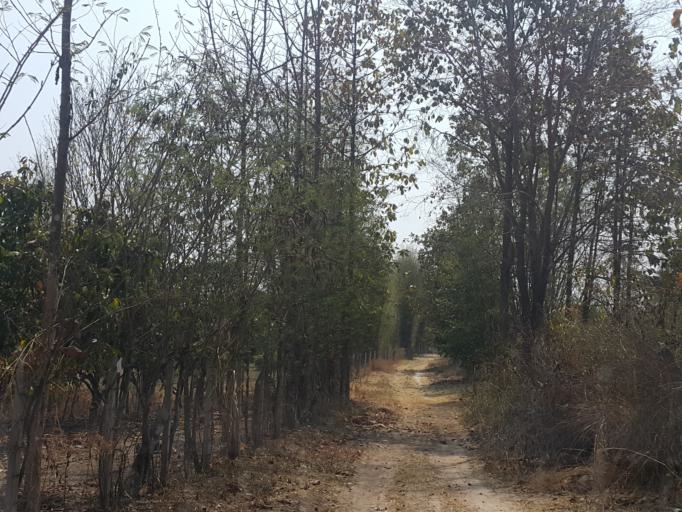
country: TH
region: Chiang Mai
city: Hang Dong
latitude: 18.6813
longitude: 98.8726
